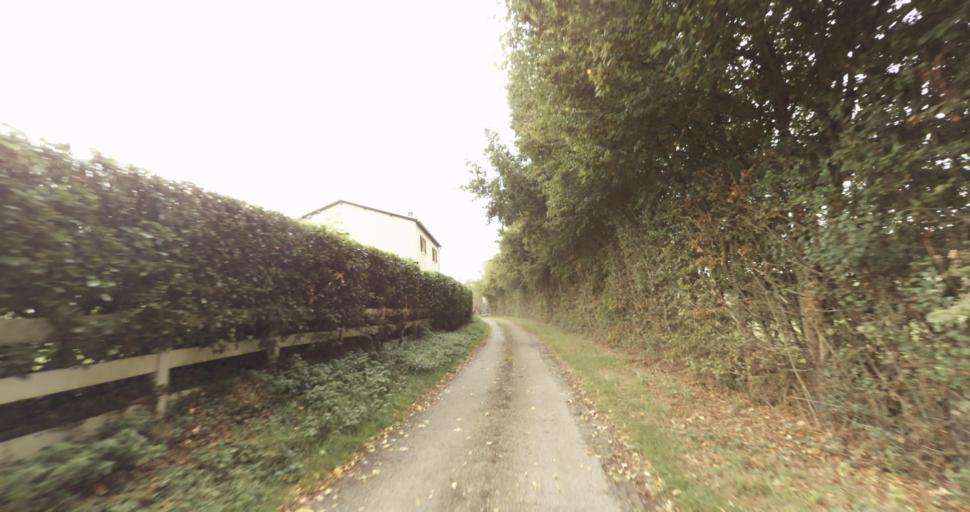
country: FR
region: Lower Normandy
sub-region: Departement de l'Orne
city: Vimoutiers
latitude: 48.8955
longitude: 0.1895
